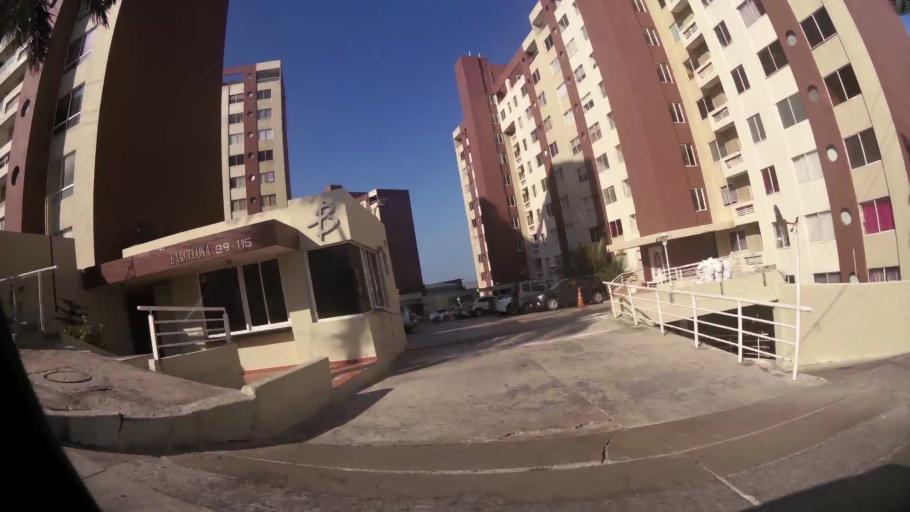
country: CO
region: Atlantico
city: Barranquilla
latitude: 11.0045
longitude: -74.8351
